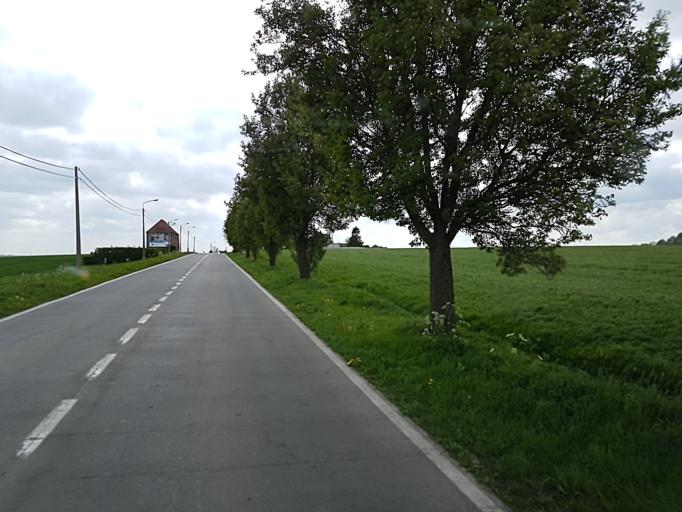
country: BE
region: Wallonia
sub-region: Province du Hainaut
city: Celles
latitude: 50.6548
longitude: 3.4338
